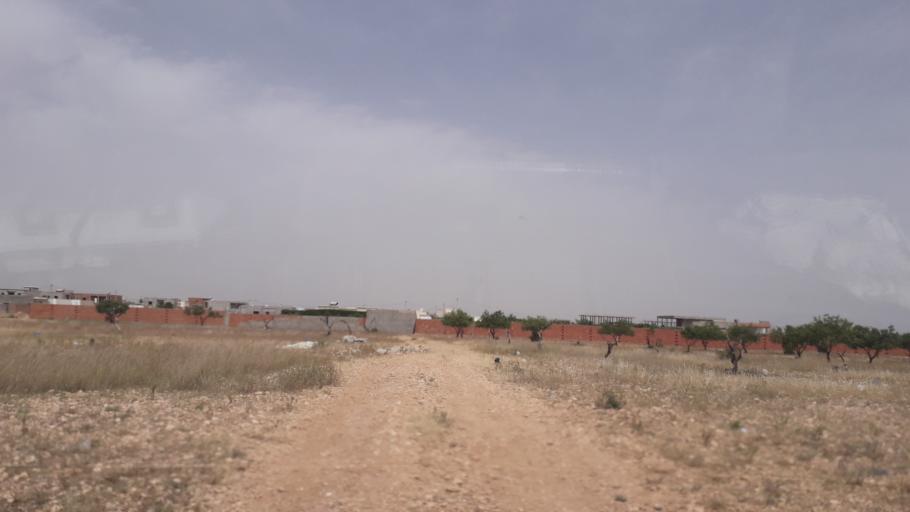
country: TN
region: Safaqis
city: Al Qarmadah
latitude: 34.8400
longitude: 10.7797
